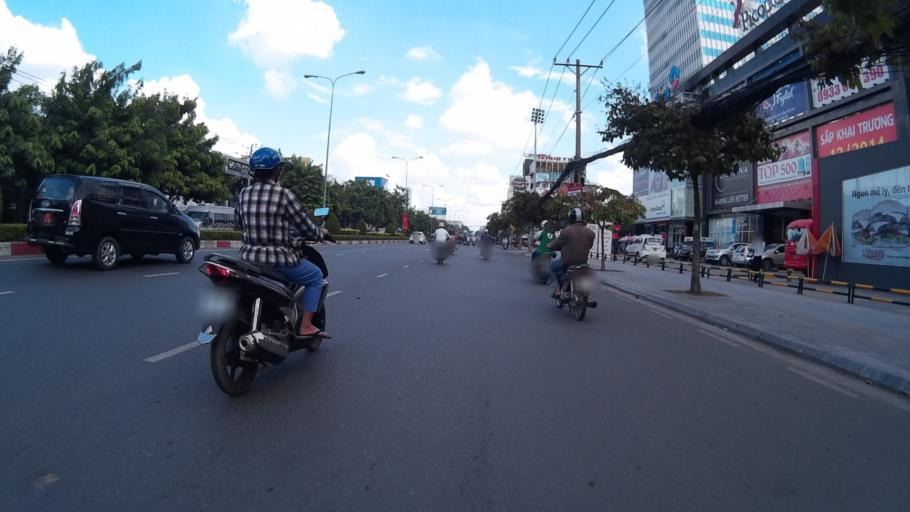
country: VN
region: Ho Chi Minh City
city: Quan Tan Phu
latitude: 10.8013
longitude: 106.6529
